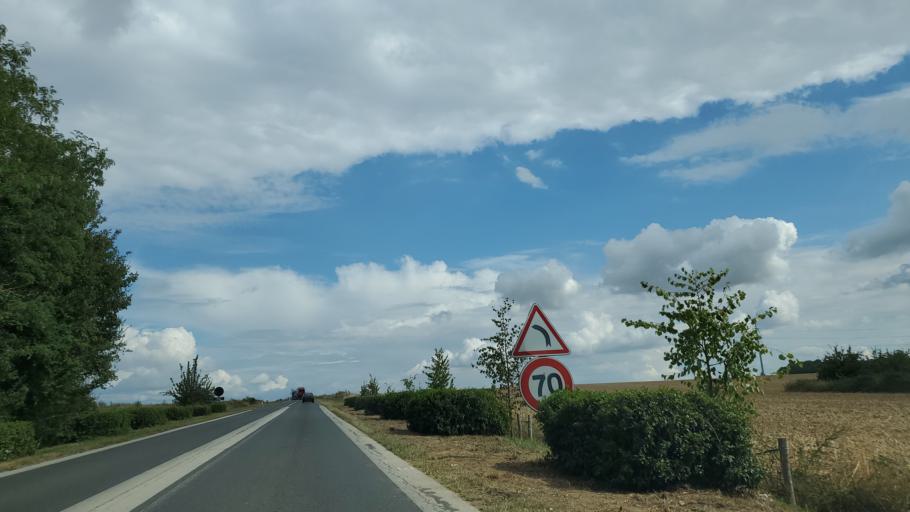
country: FR
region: Ile-de-France
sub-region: Departement de Seine-et-Marne
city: Chailly-en-Brie
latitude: 48.7882
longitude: 3.1288
